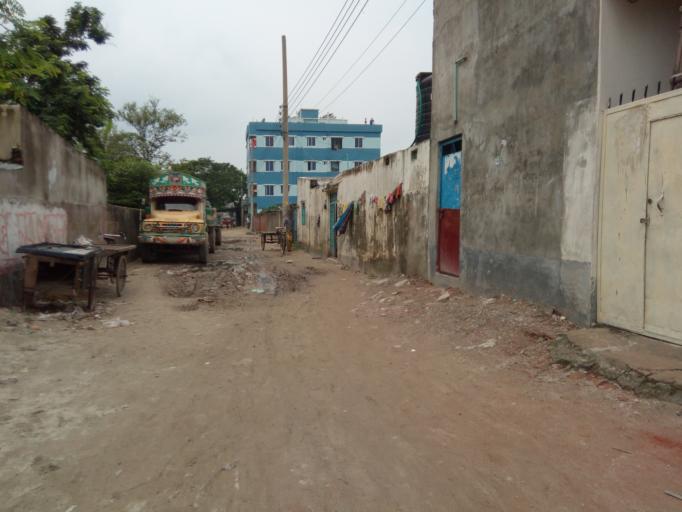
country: BD
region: Dhaka
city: Azimpur
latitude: 23.7584
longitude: 90.3521
